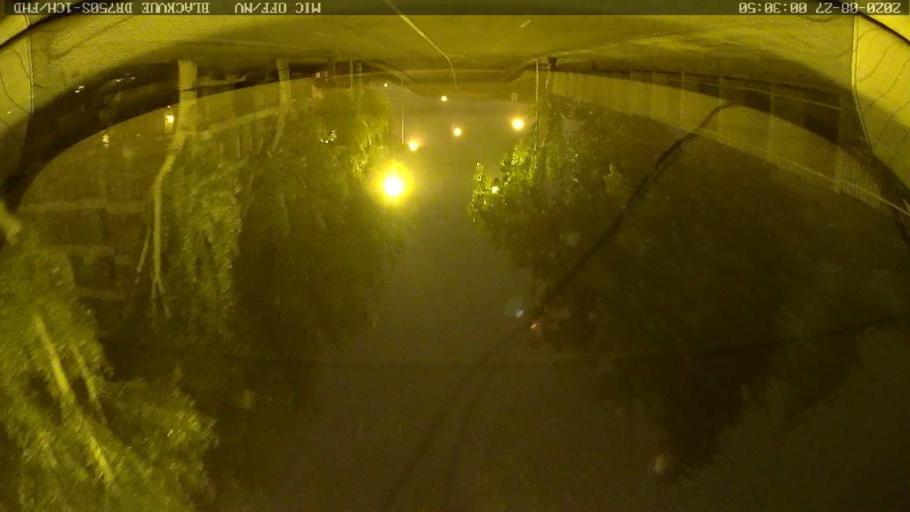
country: PT
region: Aveiro
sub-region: Aveiro
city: Aveiro
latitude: 40.6353
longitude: -8.6457
